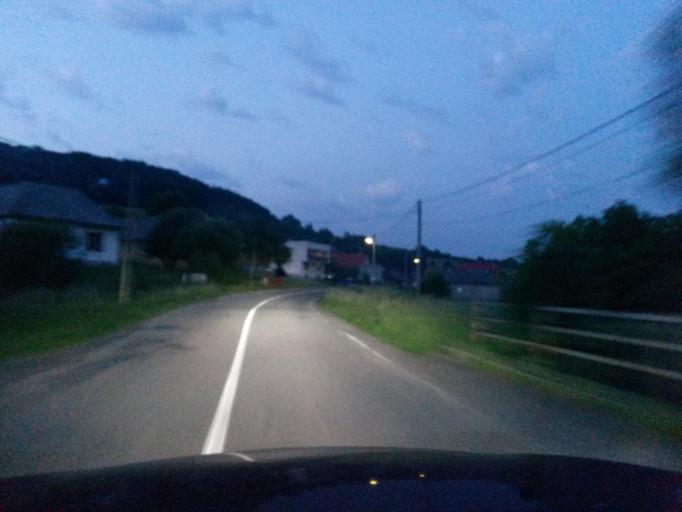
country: UA
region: Zakarpattia
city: Velykyi Bereznyi
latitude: 48.9268
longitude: 22.3023
